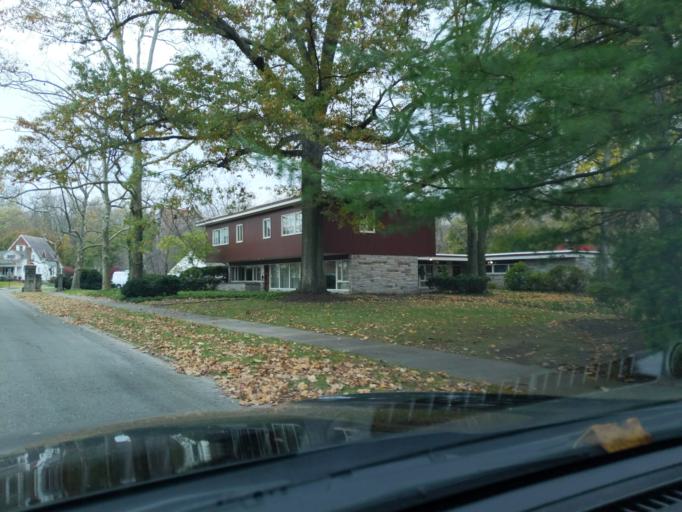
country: US
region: Pennsylvania
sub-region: Blair County
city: Lakemont
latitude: 40.4904
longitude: -78.4066
